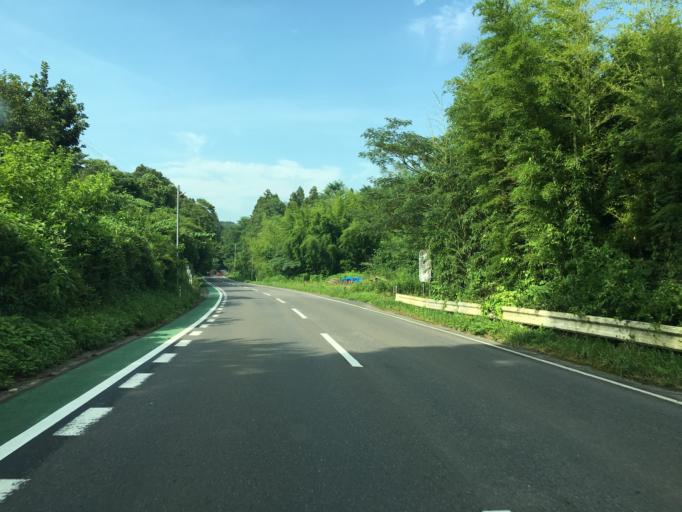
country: JP
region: Fukushima
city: Koriyama
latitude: 37.3752
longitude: 140.4461
